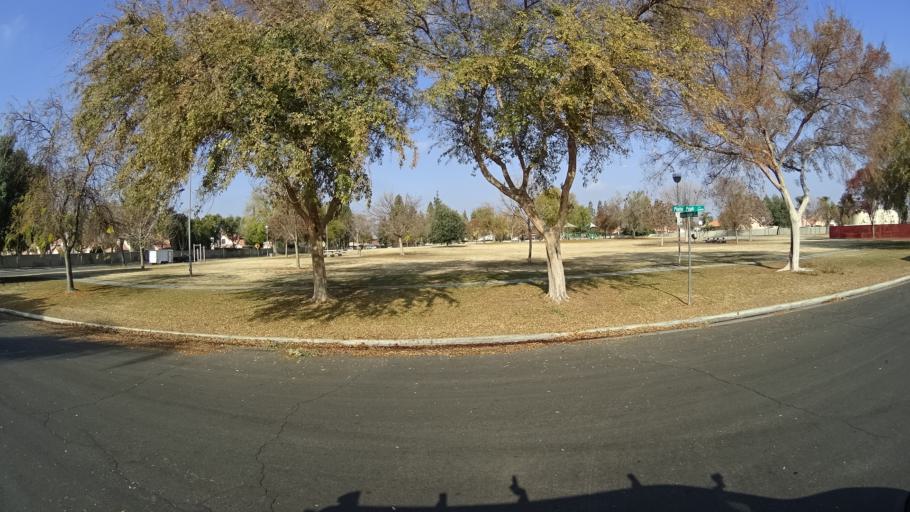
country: US
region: California
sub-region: Kern County
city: Greenacres
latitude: 35.3017
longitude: -119.0884
